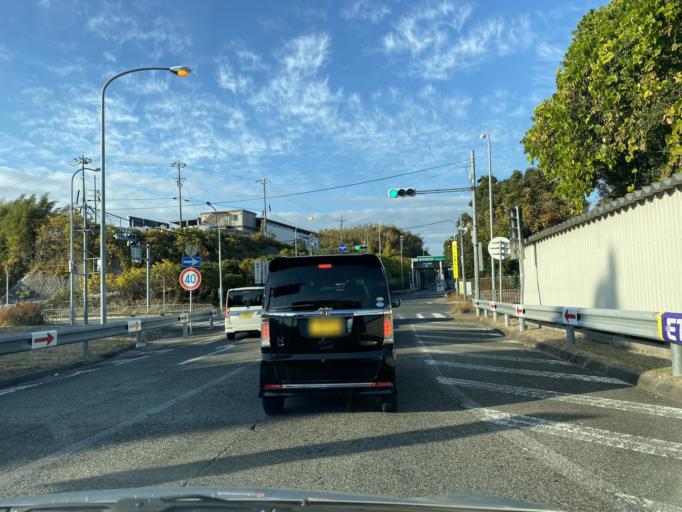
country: JP
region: Osaka
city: Izumi
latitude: 34.4380
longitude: 135.4441
